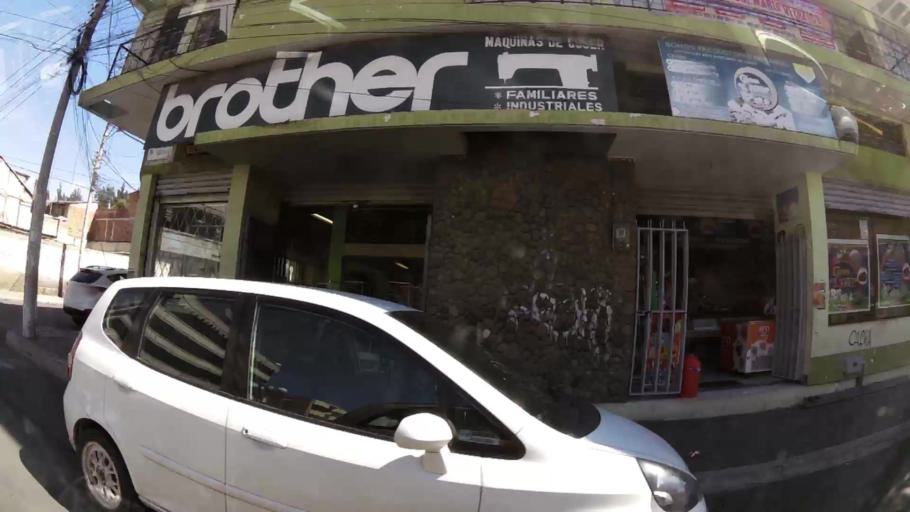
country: EC
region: Chimborazo
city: Riobamba
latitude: -1.6683
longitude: -78.6528
